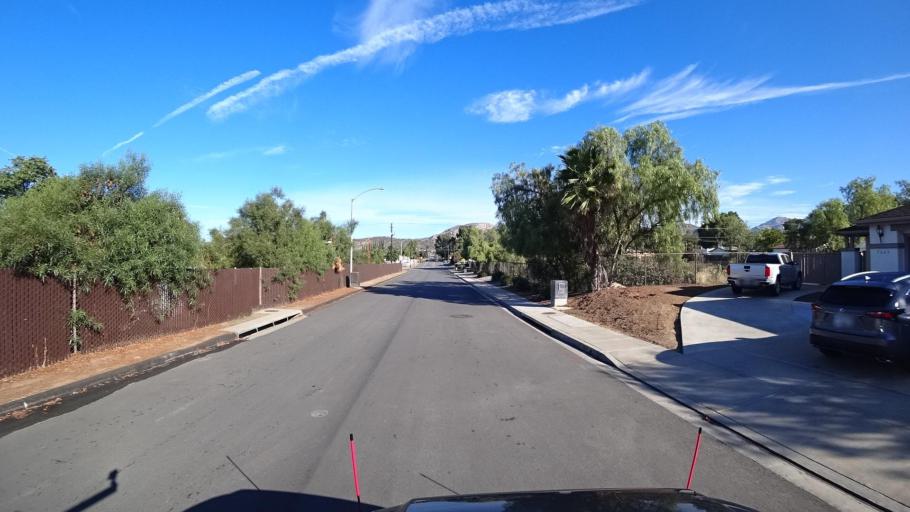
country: US
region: California
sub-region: San Diego County
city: Lakeside
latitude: 32.8557
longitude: -116.9082
